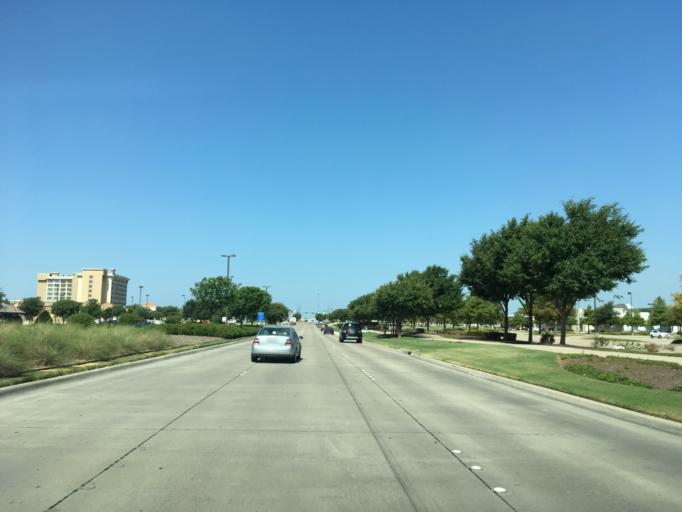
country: US
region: Texas
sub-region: Collin County
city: Allen
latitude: 33.1298
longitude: -96.6506
